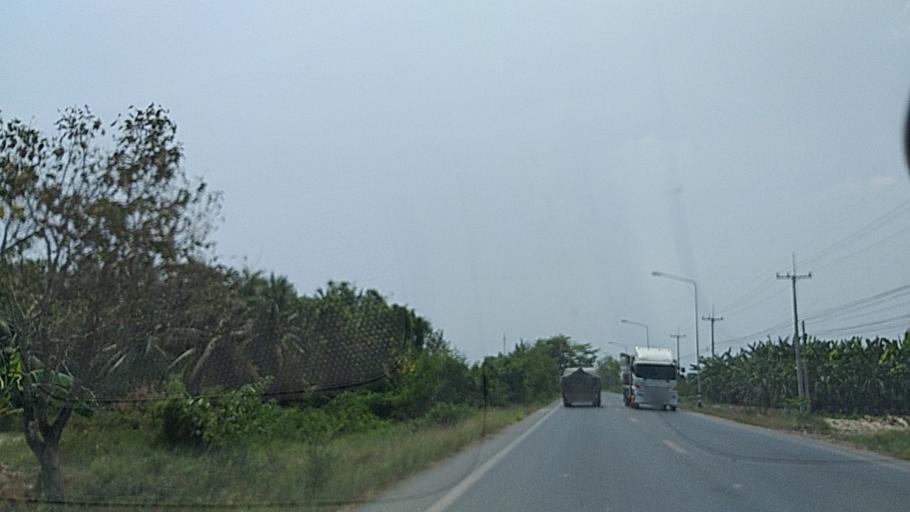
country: TH
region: Chachoengsao
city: Bang Nam Priao
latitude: 13.9328
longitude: 100.9774
